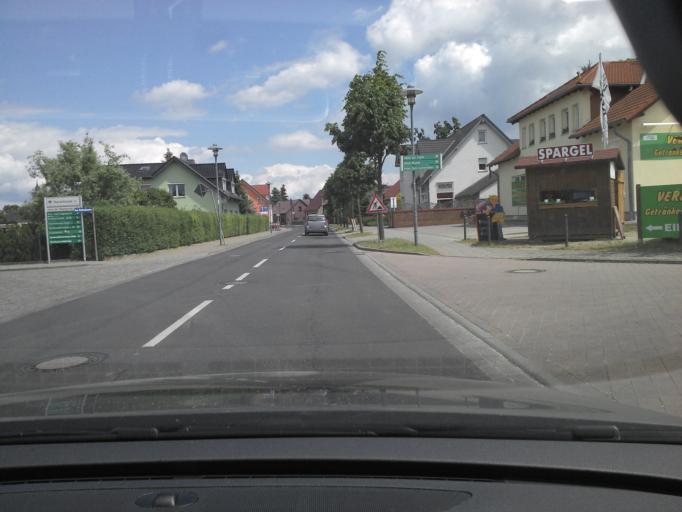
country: DE
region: Brandenburg
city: Burg
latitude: 51.8294
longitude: 14.1470
